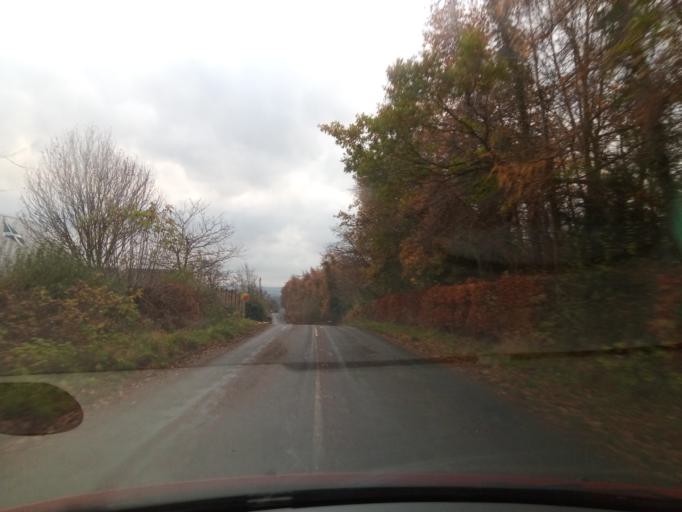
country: GB
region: Scotland
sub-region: The Scottish Borders
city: Newtown St Boswells
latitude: 55.5860
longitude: -2.6813
